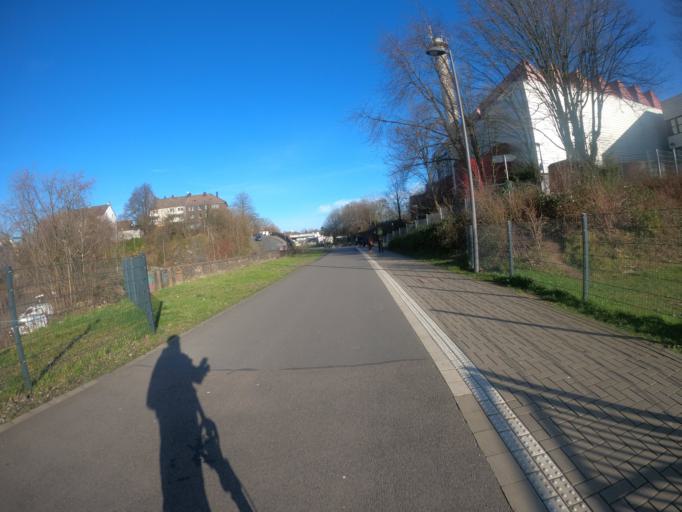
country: DE
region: North Rhine-Westphalia
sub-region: Regierungsbezirk Dusseldorf
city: Wuppertal
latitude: 51.2780
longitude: 7.2199
